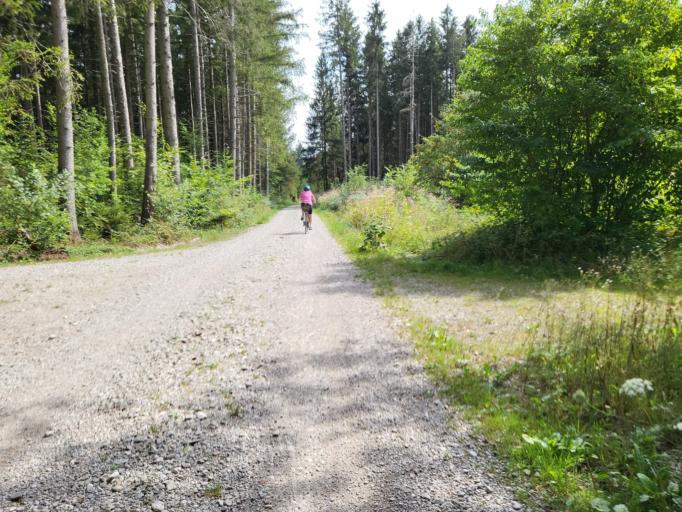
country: DE
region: Bavaria
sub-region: Upper Bavaria
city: Hohenkirchen-Siegertsbrunn
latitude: 48.0426
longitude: 11.7460
